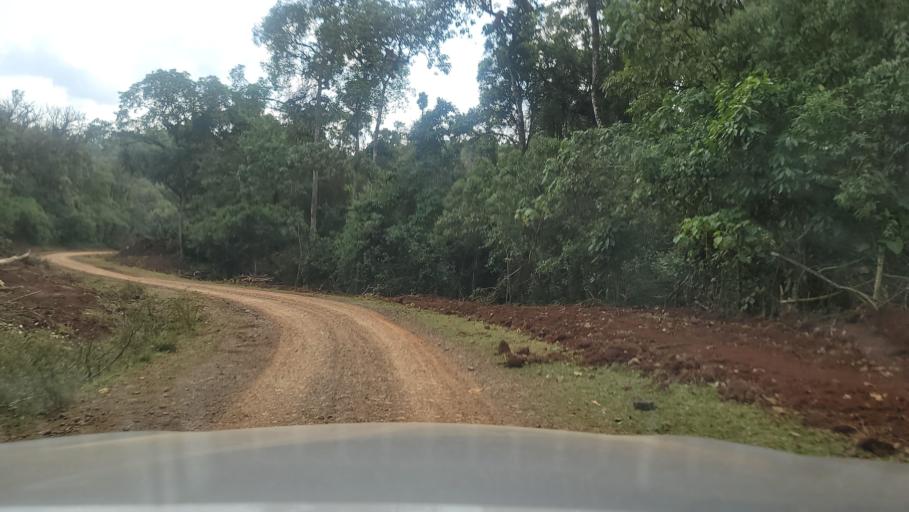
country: ET
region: Southern Nations, Nationalities, and People's Region
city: Bonga
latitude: 7.6734
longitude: 36.2423
